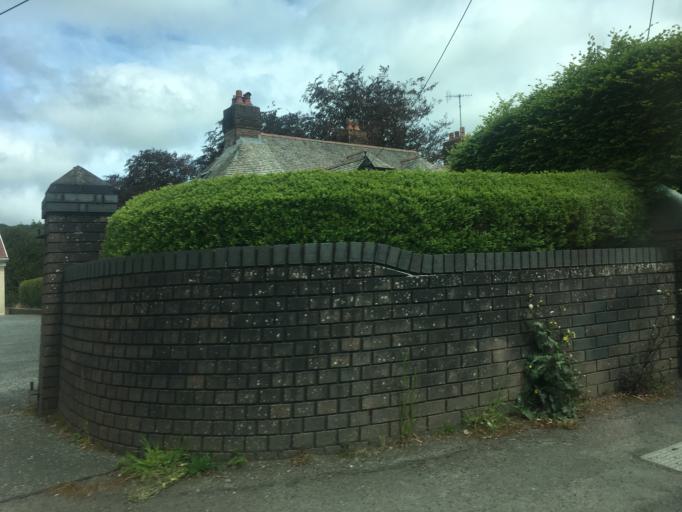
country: GB
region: Wales
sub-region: County of Ceredigion
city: Lampeter
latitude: 52.1187
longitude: -4.0789
